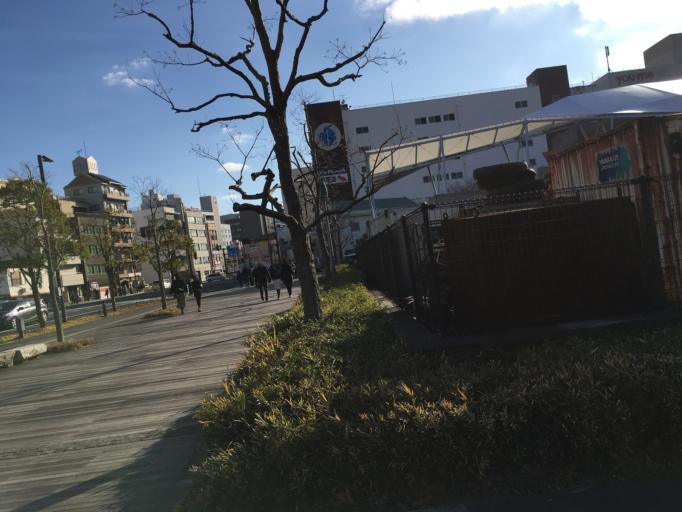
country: JP
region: Nagasaki
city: Nagasaki-shi
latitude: 32.7477
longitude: 129.8709
